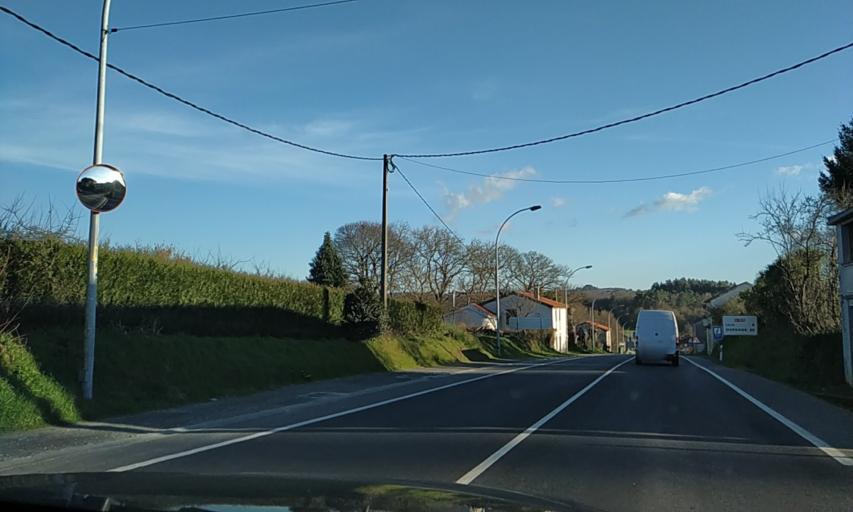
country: ES
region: Galicia
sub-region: Provincia de Pontevedra
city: Lalin
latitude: 42.6784
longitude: -8.1658
